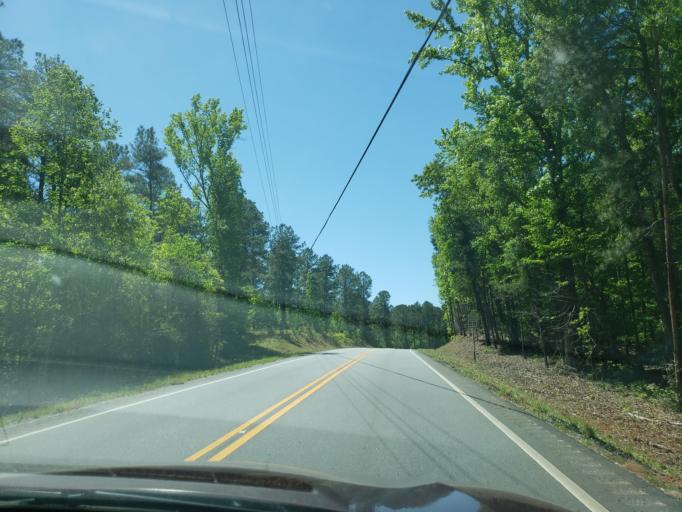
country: US
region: Alabama
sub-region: Tallapoosa County
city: Dadeville
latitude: 32.7077
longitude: -85.7853
